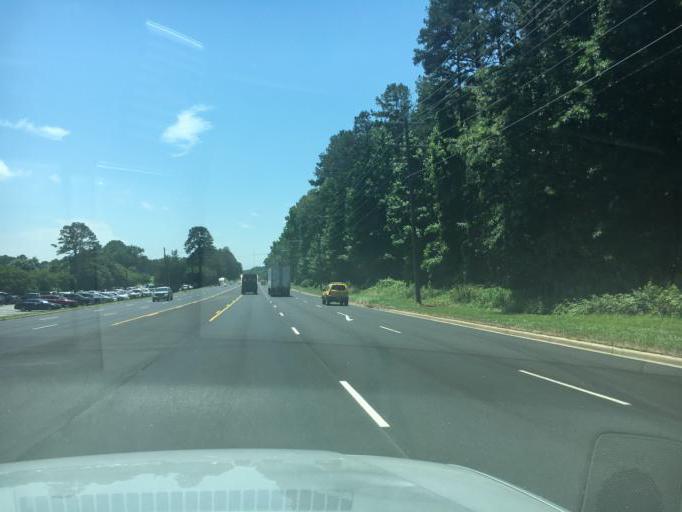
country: US
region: South Carolina
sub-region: Greenville County
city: Travelers Rest
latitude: 34.9341
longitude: -82.4488
